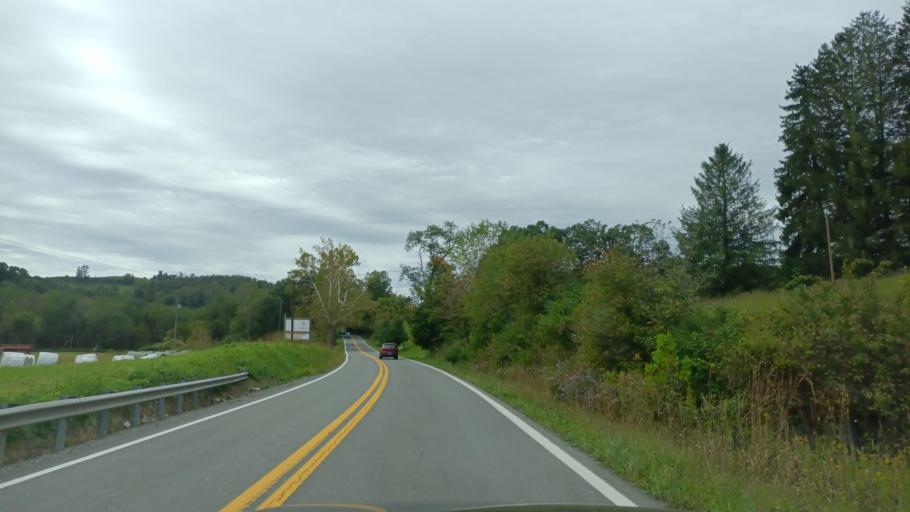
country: US
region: West Virginia
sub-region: Taylor County
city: Grafton
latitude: 39.3368
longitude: -79.8625
